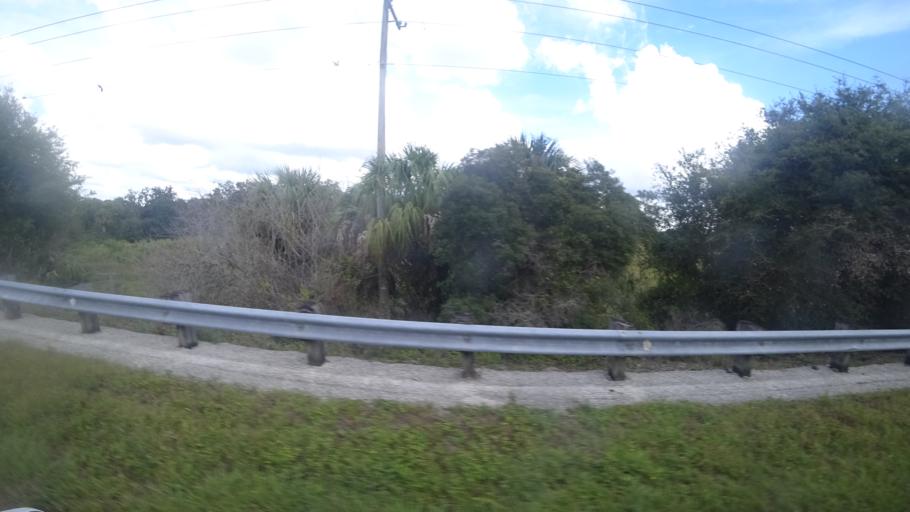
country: US
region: Florida
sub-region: Hillsborough County
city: Ruskin
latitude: 27.6553
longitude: -82.4317
